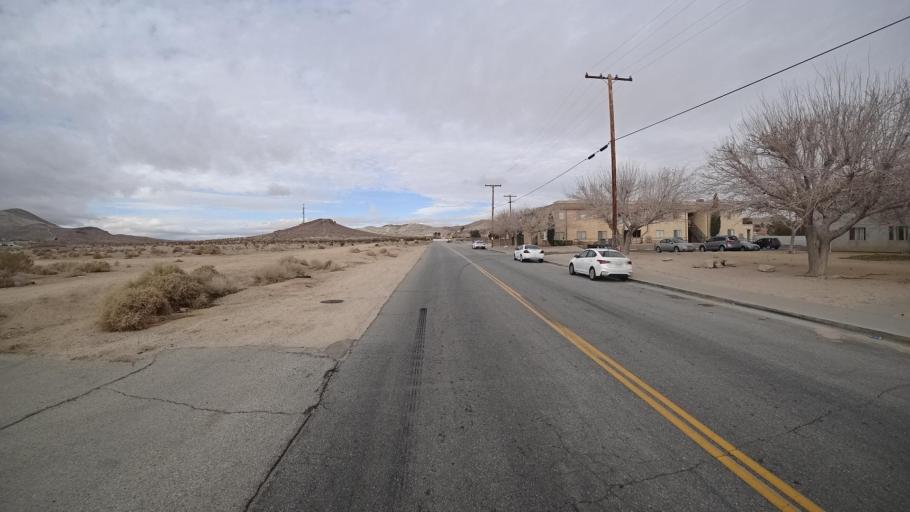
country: US
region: California
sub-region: Kern County
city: Rosamond
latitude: 34.8715
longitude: -118.1584
